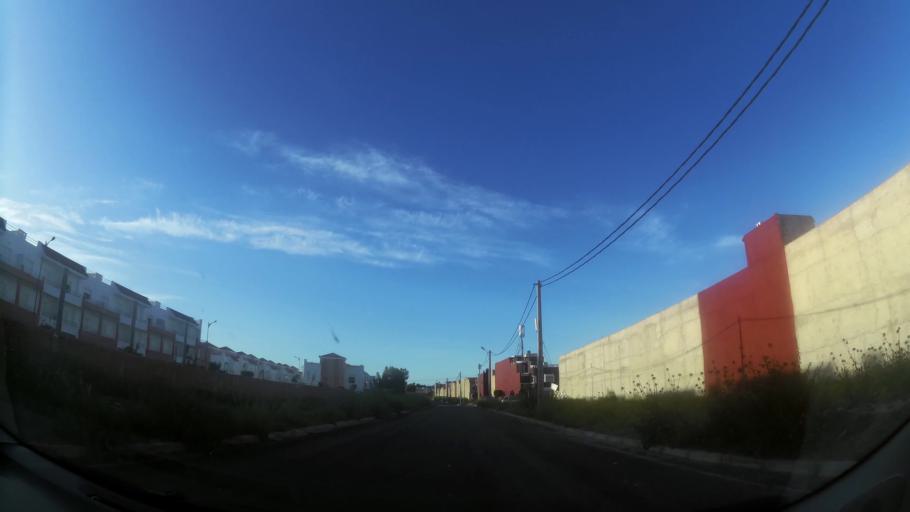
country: MA
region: Oriental
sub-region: Berkane-Taourirt
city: Madagh
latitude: 35.0808
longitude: -2.2408
